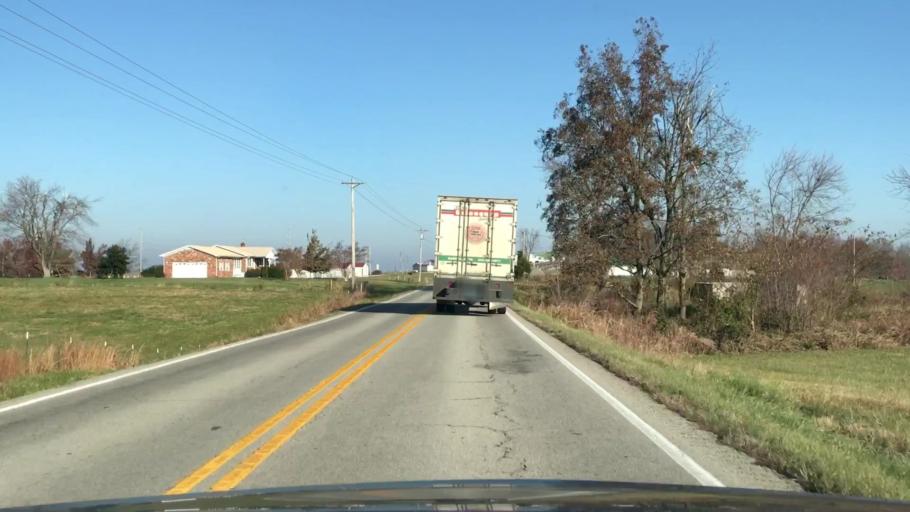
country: US
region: Kentucky
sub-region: Grayson County
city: Leitchfield
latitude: 37.4001
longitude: -86.2372
